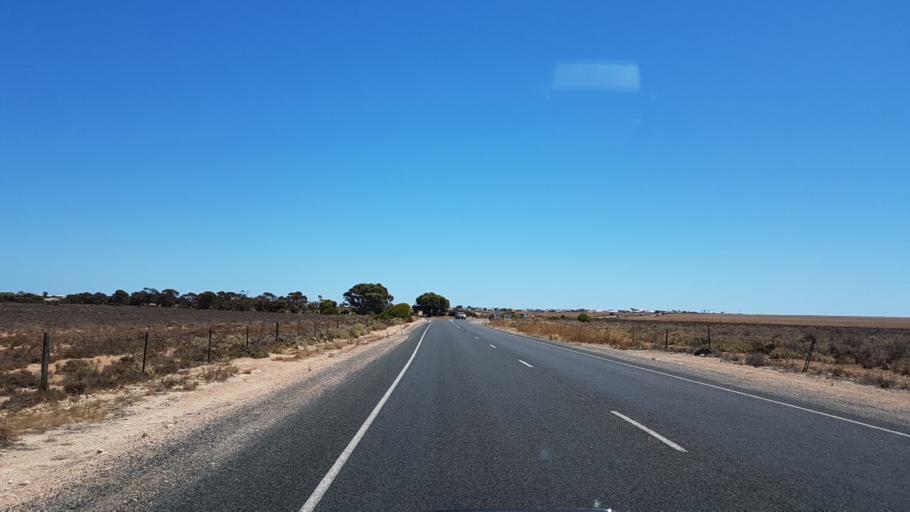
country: AU
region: South Australia
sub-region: Copper Coast
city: Wallaroo
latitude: -33.9089
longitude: 137.6416
